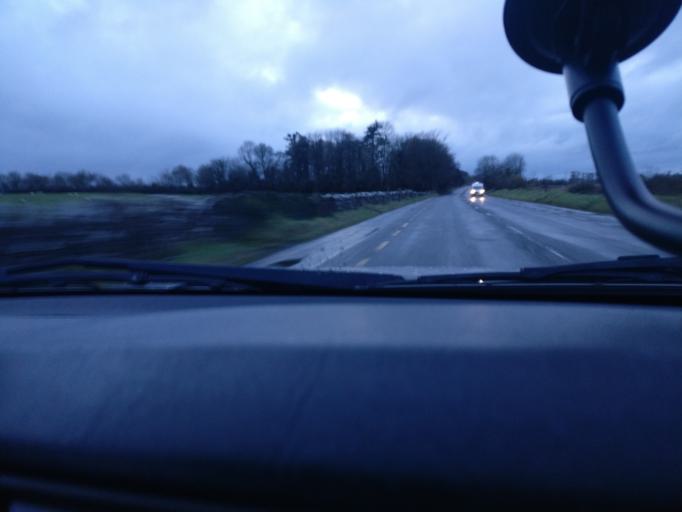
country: IE
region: Connaught
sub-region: County Galway
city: Loughrea
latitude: 53.2216
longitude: -8.4667
